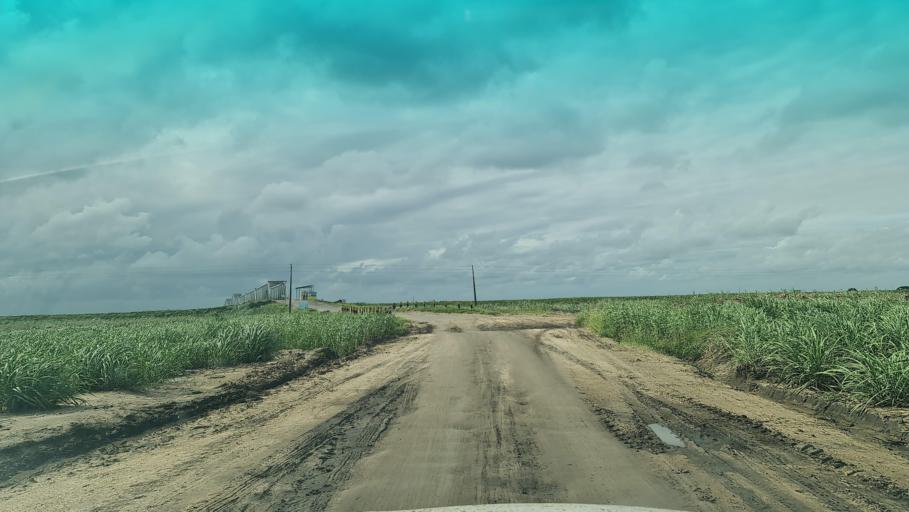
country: MZ
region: Maputo
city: Manhica
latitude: -25.4758
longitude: 32.8136
